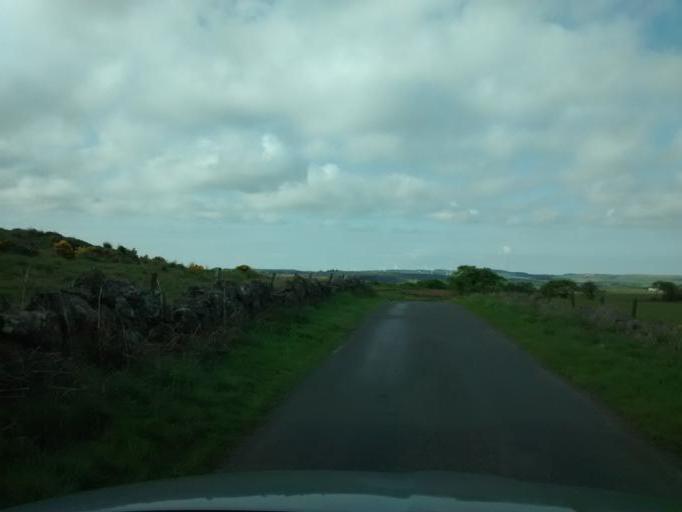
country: GB
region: Scotland
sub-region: North Lanarkshire
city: Harthill
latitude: 55.8944
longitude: -3.7555
